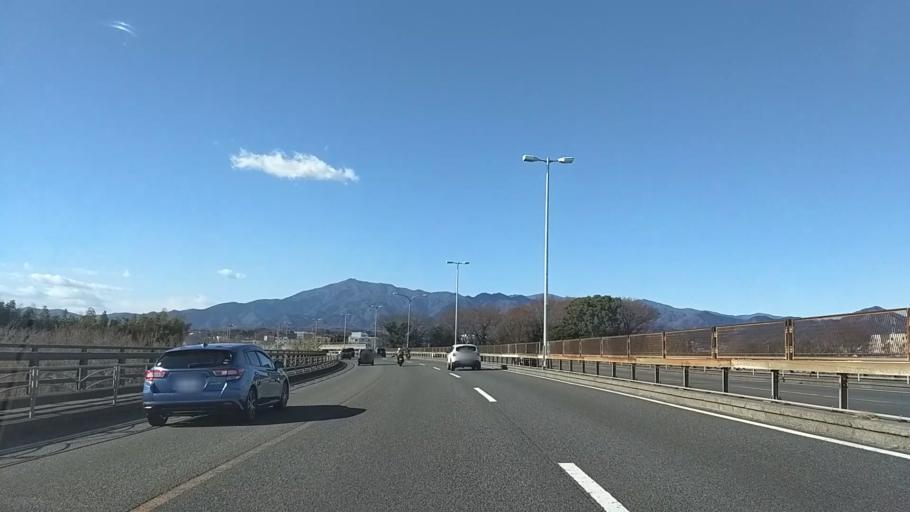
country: JP
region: Kanagawa
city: Atsugi
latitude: 35.4655
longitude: 139.3661
